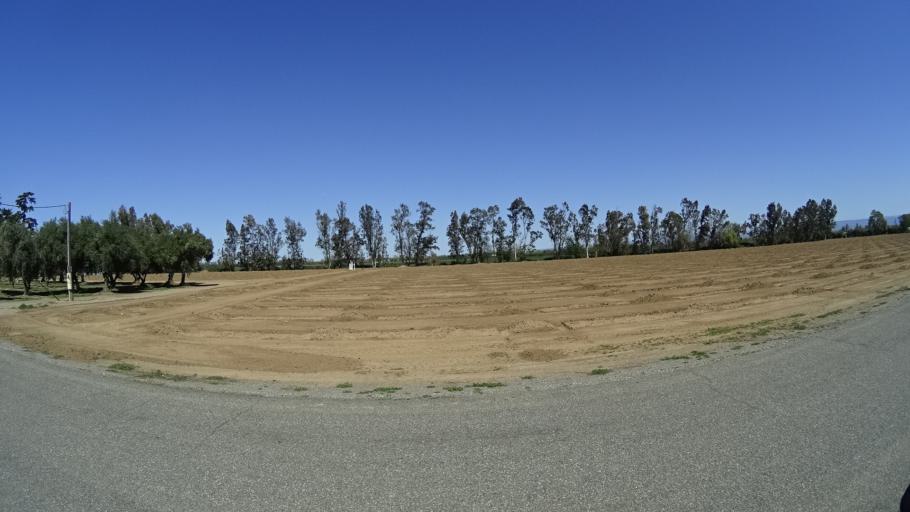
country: US
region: California
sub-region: Glenn County
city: Hamilton City
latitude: 39.7969
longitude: -122.0756
